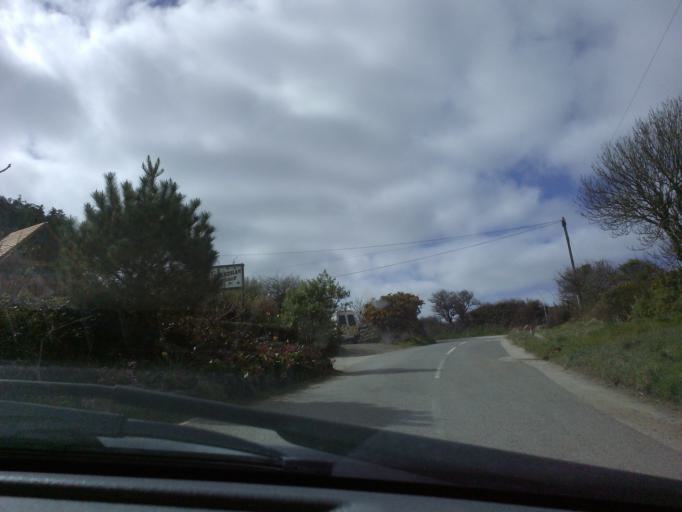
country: GB
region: England
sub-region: Cornwall
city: St. Buryan
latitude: 50.0585
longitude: -5.6089
